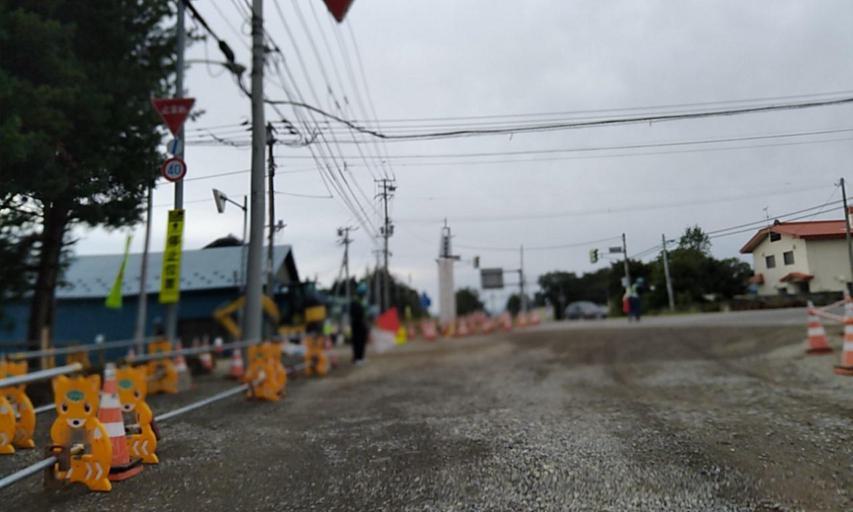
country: JP
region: Hokkaido
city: Obihiro
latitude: 42.8357
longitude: 143.1911
